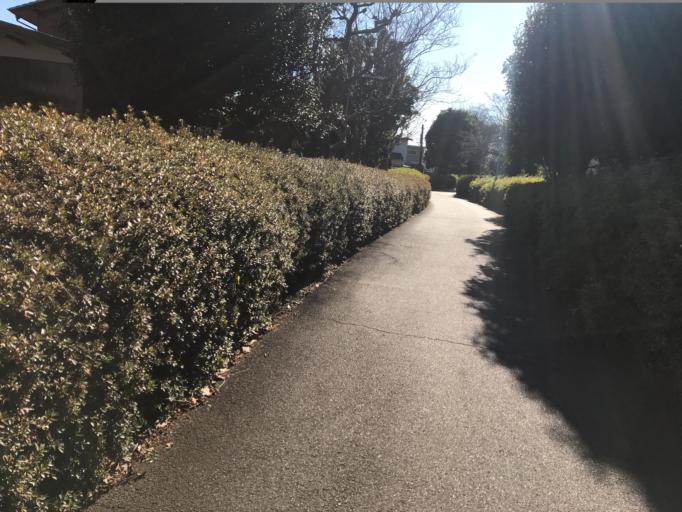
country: JP
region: Tokyo
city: Kokubunji
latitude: 35.7072
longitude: 139.4323
